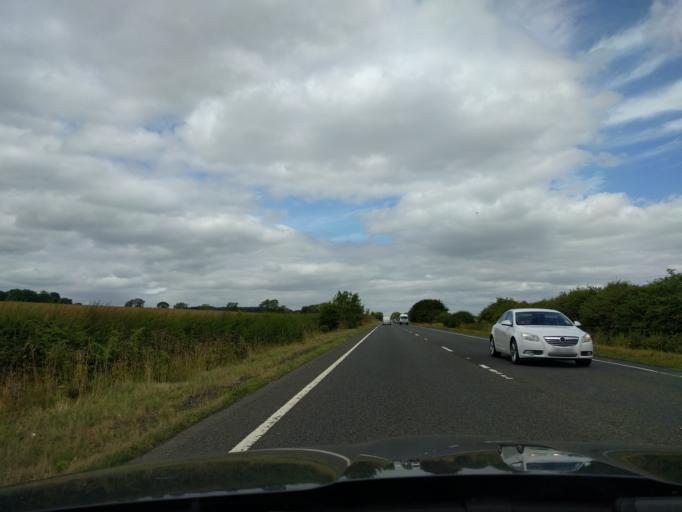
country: GB
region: England
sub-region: Northumberland
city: Alnwick
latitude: 55.4388
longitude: -1.6953
